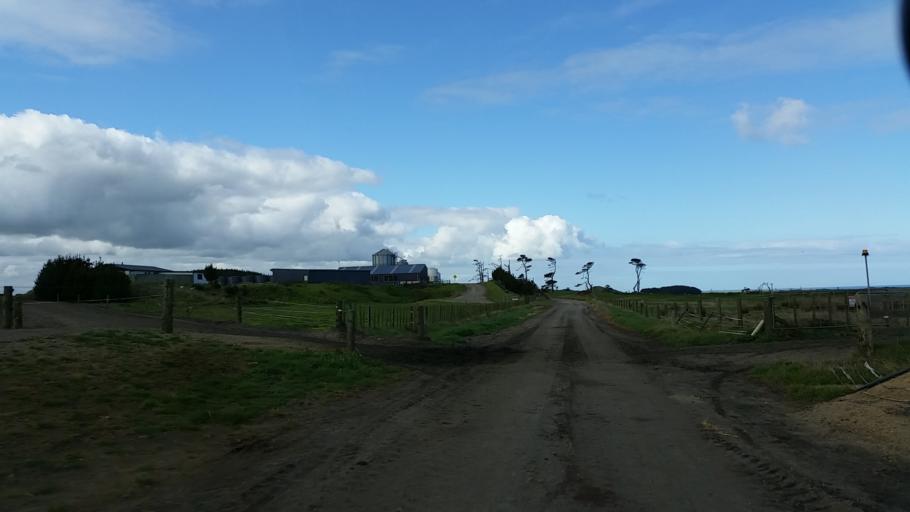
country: NZ
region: Taranaki
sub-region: South Taranaki District
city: Patea
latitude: -39.7984
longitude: 174.5938
